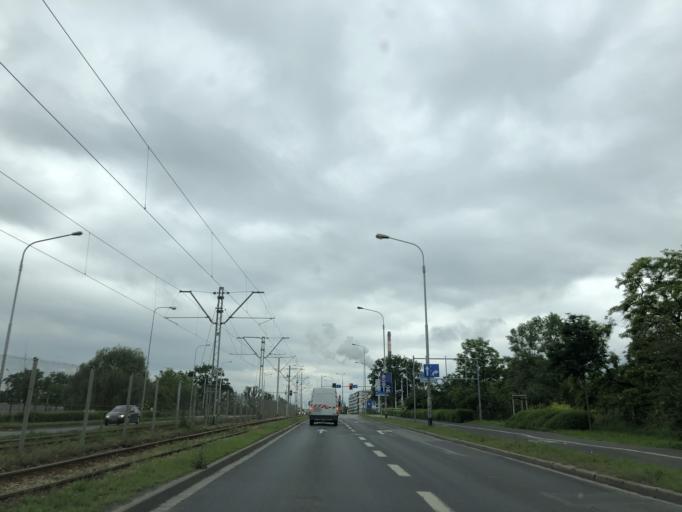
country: PL
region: Lower Silesian Voivodeship
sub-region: Powiat wroclawski
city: Wroclaw
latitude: 51.1343
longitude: 17.0283
